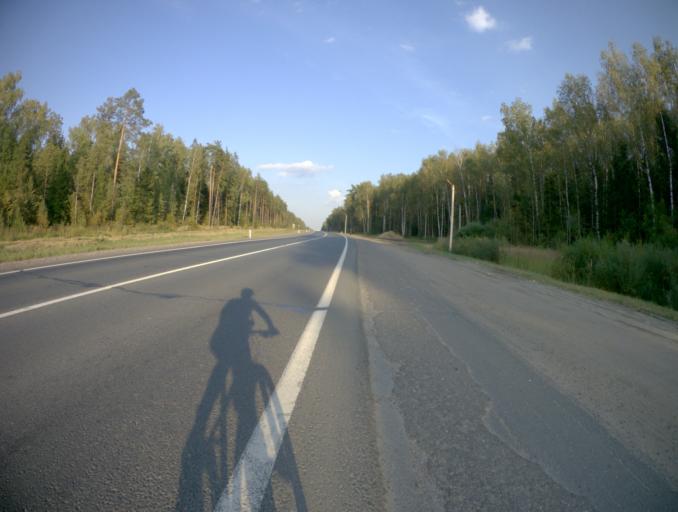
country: RU
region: Vladimir
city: Kameshkovo
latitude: 56.1932
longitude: 40.9303
